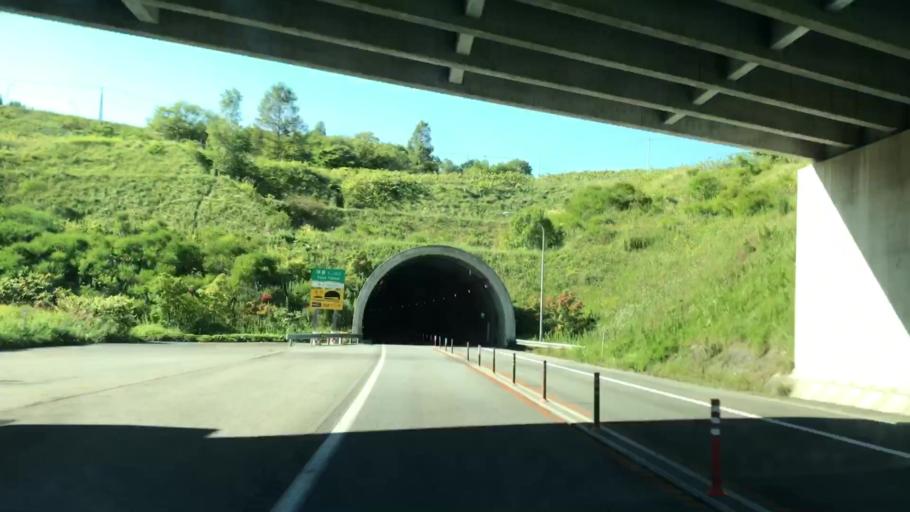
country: JP
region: Hokkaido
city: Date
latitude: 42.5520
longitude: 140.7886
